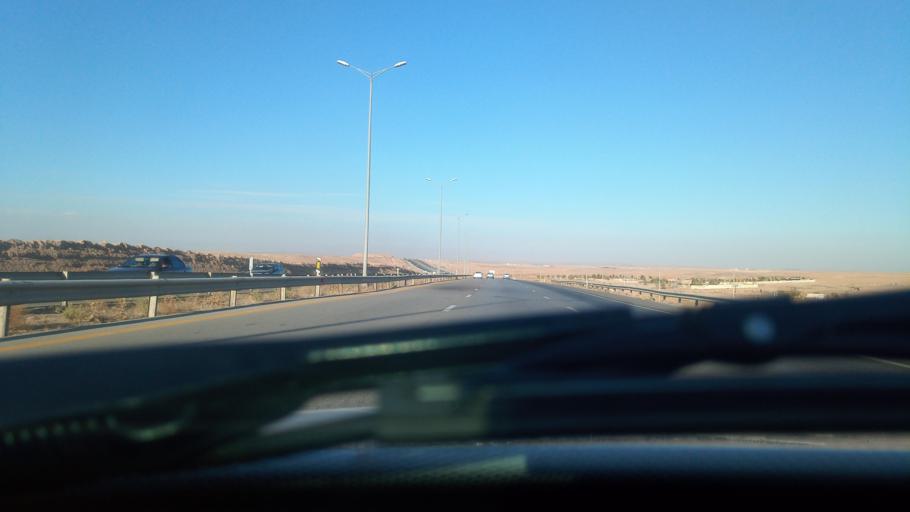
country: IR
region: Razavi Khorasan
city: Mashhad
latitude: 36.0562
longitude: 59.7168
